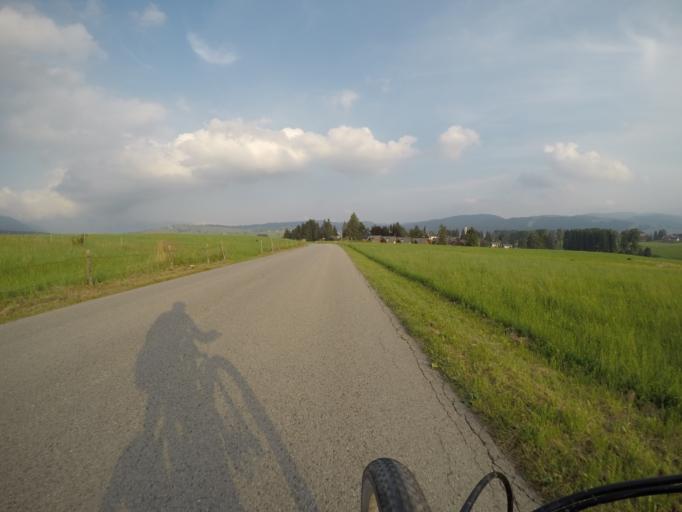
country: IT
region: Veneto
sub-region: Provincia di Vicenza
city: Asiago
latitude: 45.8838
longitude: 11.5018
